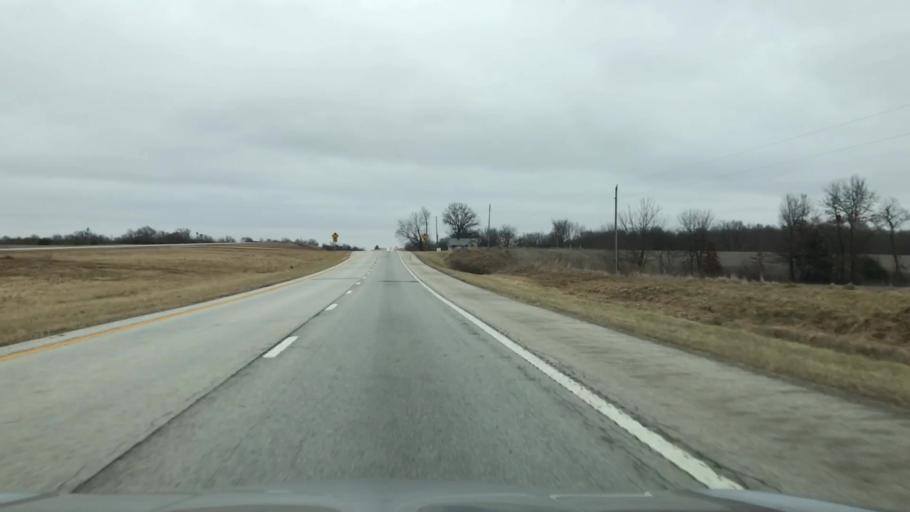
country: US
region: Missouri
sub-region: Linn County
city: Marceline
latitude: 39.7600
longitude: -92.9161
